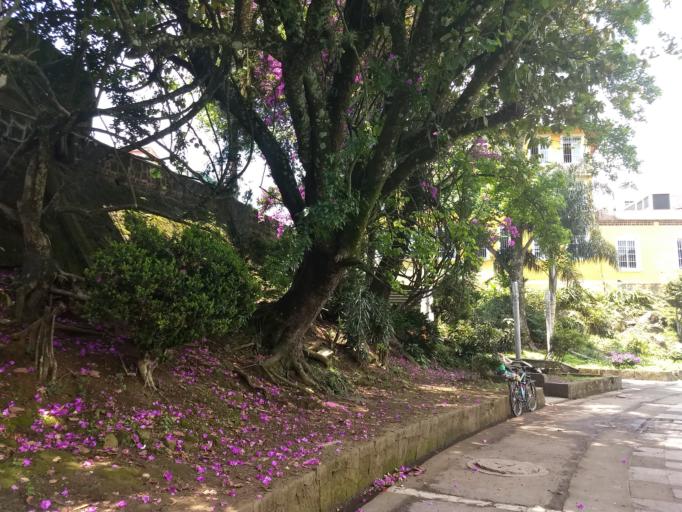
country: MX
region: Veracruz
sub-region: Xalapa
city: Xalapa de Enriquez
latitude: 19.5219
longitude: -96.9236
